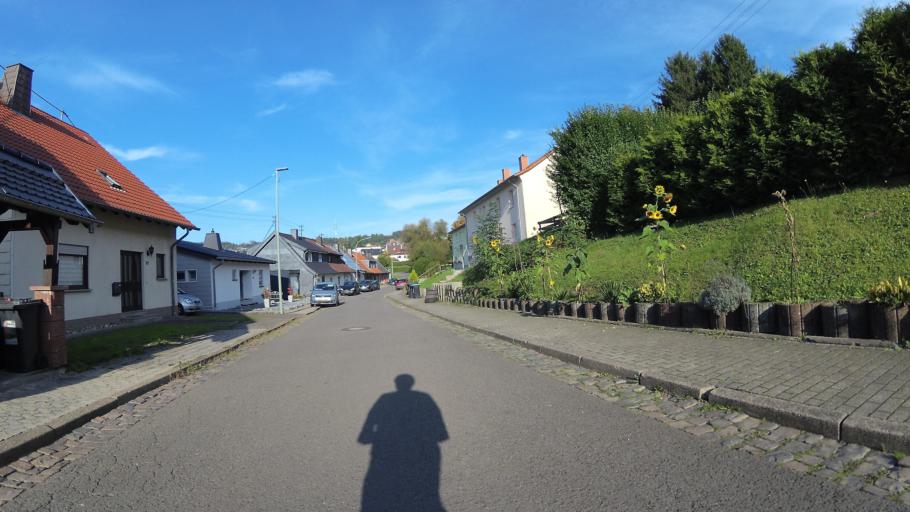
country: DE
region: Saarland
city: Friedrichsthal
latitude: 49.3173
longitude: 7.0918
